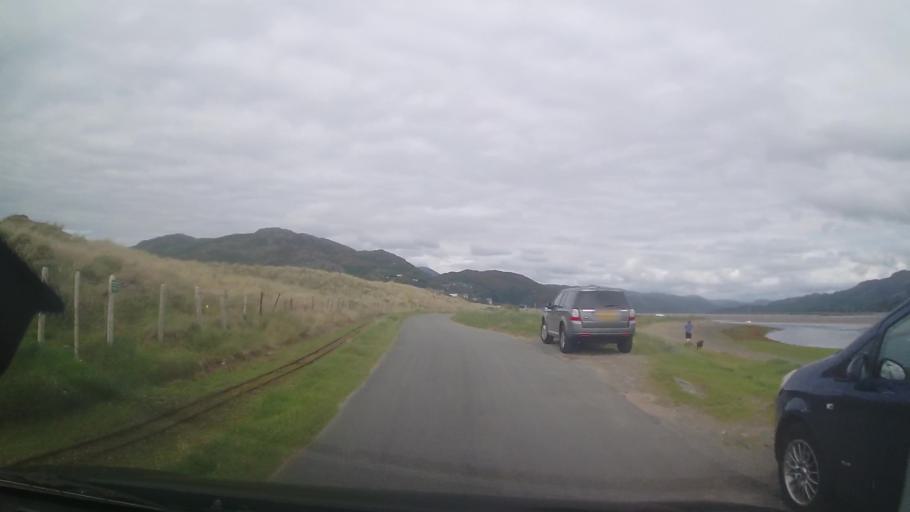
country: GB
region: Wales
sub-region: Gwynedd
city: Barmouth
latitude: 52.7103
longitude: -4.0545
